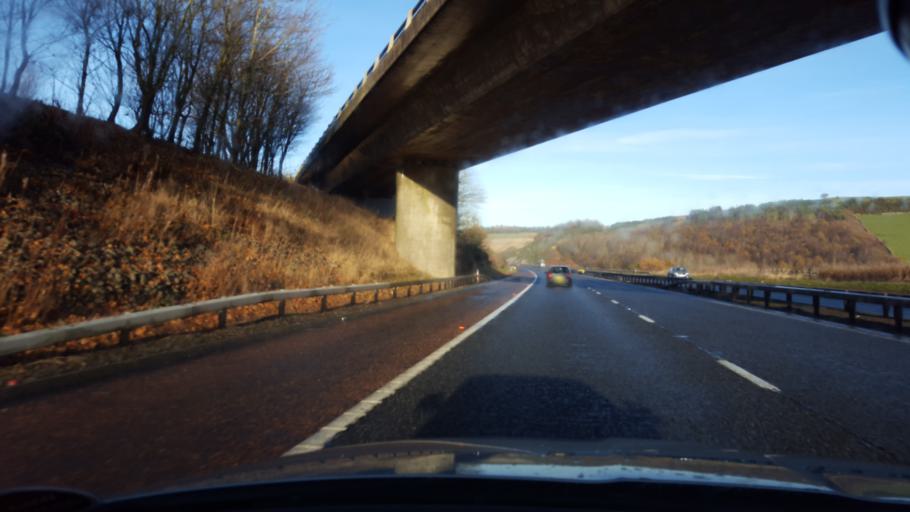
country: GB
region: Scotland
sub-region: Perth and Kinross
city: Milnathort
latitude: 56.2608
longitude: -3.3784
